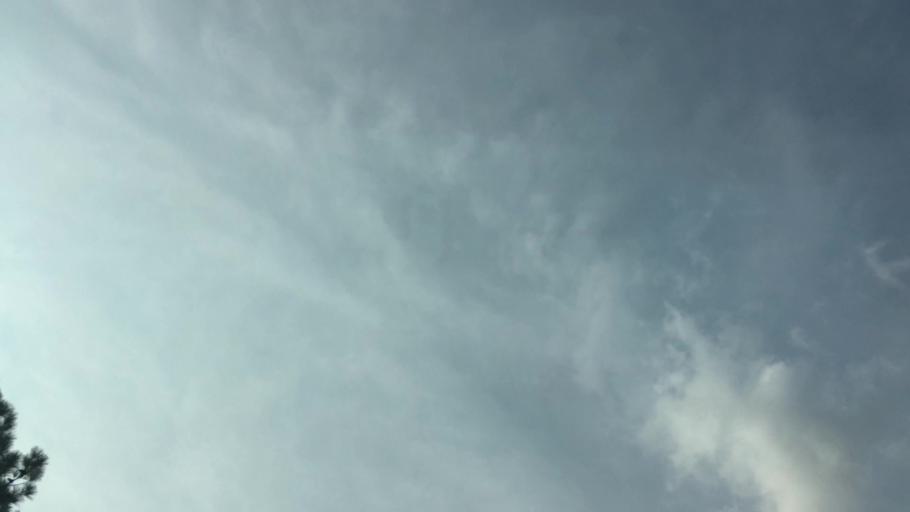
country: US
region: Alabama
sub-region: Bibb County
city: Woodstock
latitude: 33.2225
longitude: -87.1231
